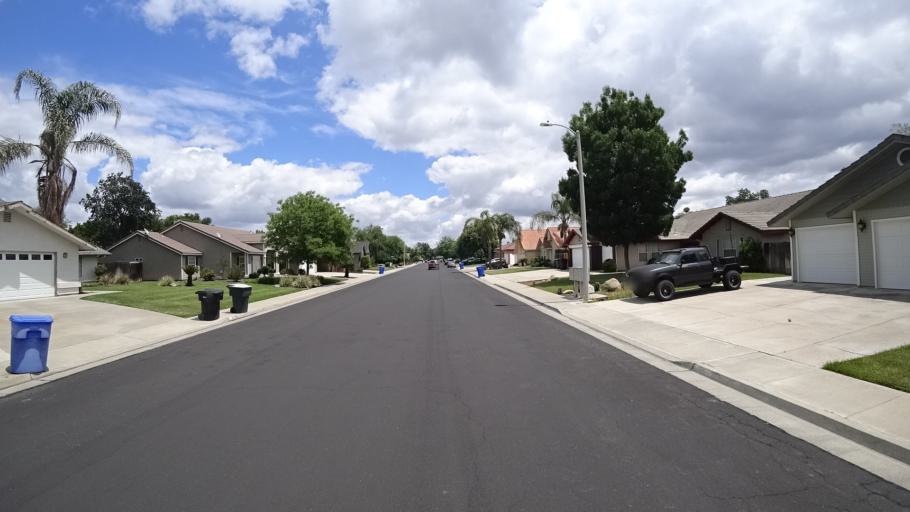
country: US
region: California
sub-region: Kings County
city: Hanford
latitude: 36.3525
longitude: -119.6522
